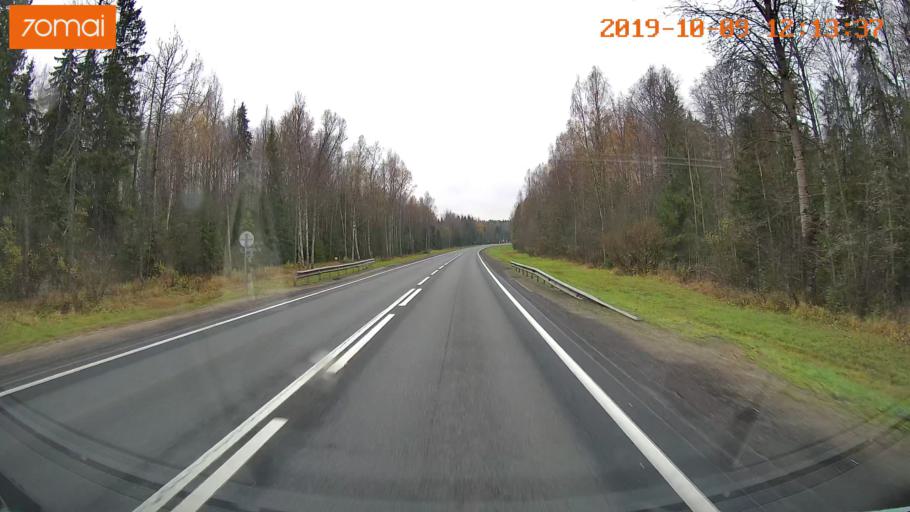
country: RU
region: Jaroslavl
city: Prechistoye
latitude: 58.5079
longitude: 40.3448
